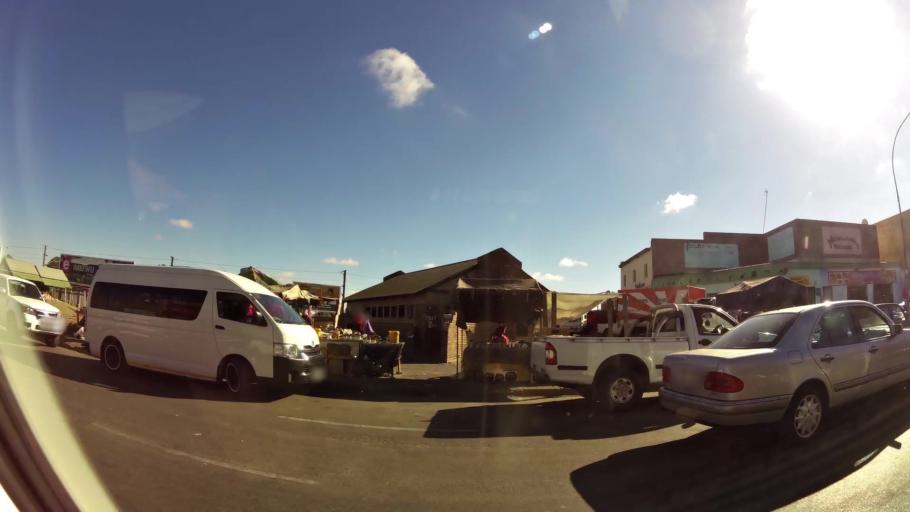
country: ZA
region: Limpopo
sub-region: Capricorn District Municipality
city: Polokwane
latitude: -23.9014
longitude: 29.4456
